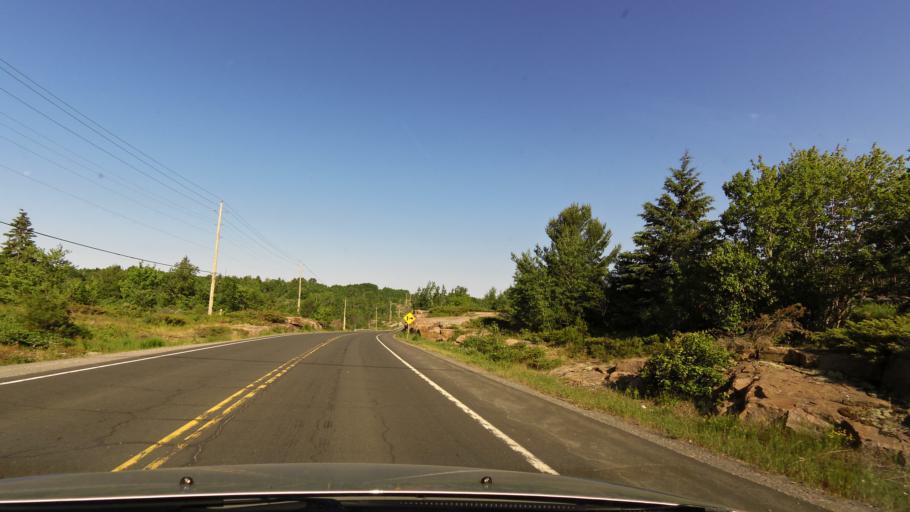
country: CA
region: Ontario
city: Greater Sudbury
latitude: 46.1047
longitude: -80.6357
